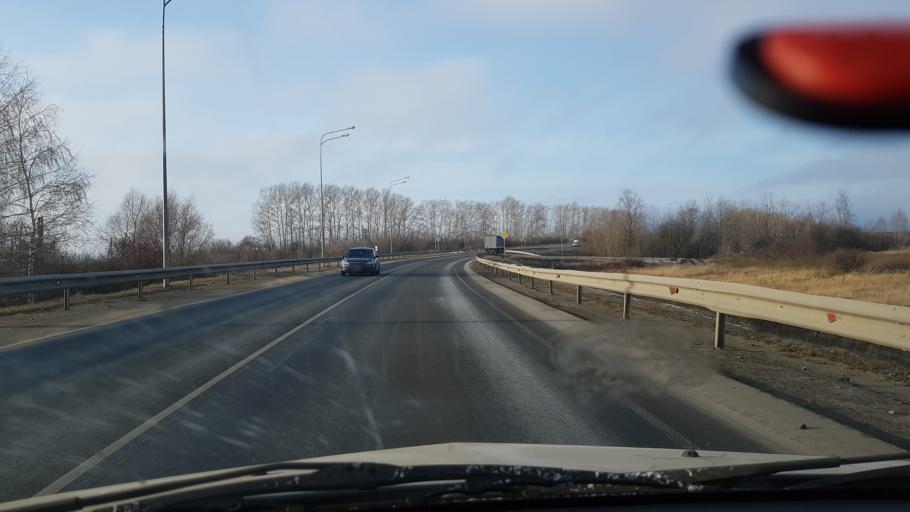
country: RU
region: Tatarstan
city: Laishevo
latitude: 55.3915
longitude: 49.7961
